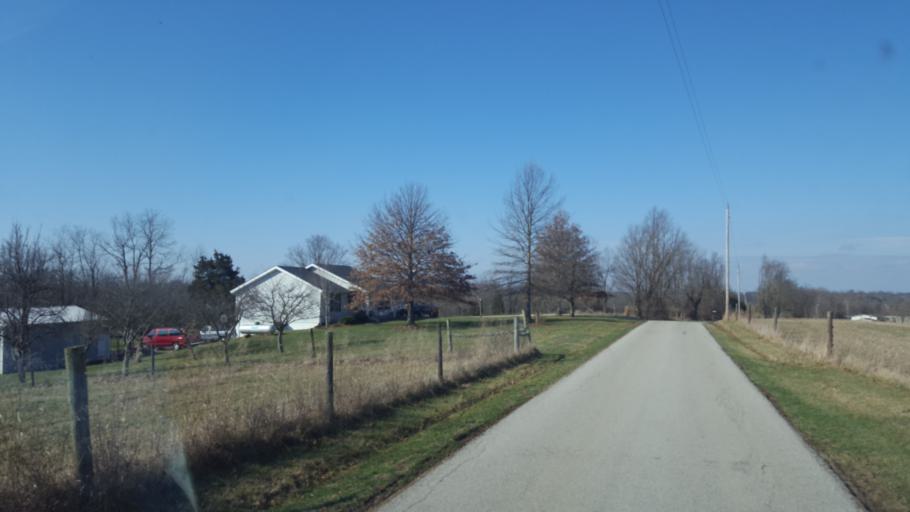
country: US
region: Kentucky
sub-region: Henry County
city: Eminence
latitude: 38.2985
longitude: -85.0356
